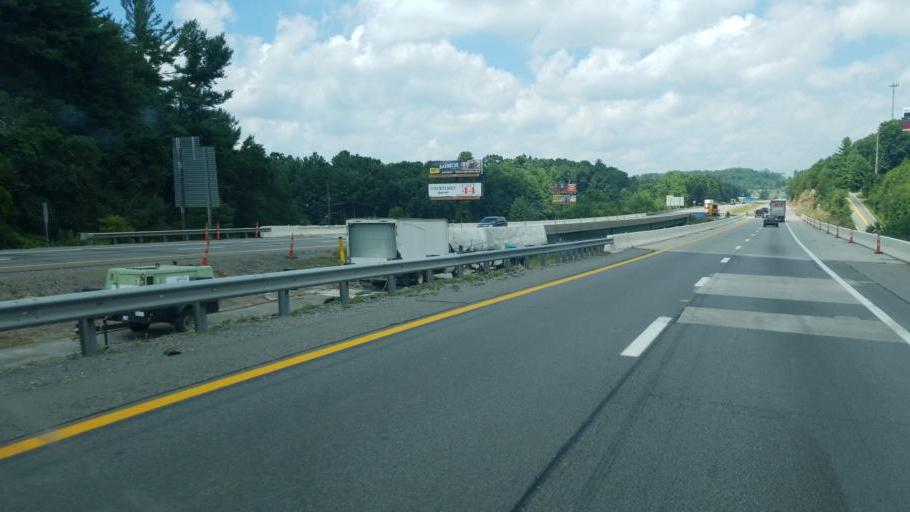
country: US
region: West Virginia
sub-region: Raleigh County
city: Mabscott
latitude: 37.7793
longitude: -81.2209
